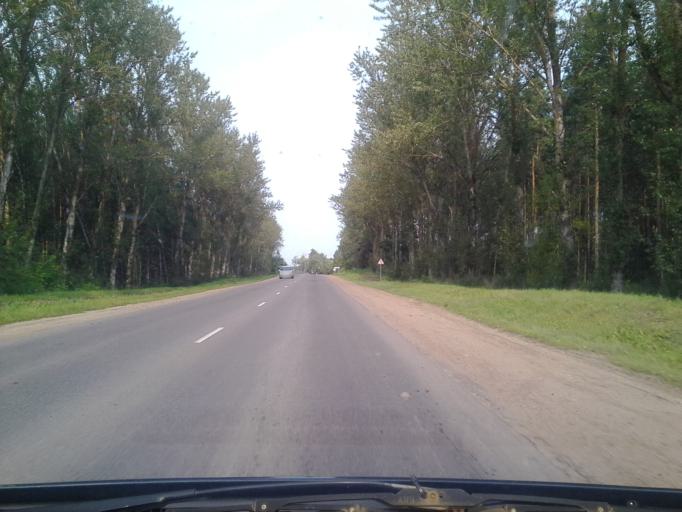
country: BY
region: Minsk
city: Hatava
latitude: 53.8127
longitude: 27.6471
